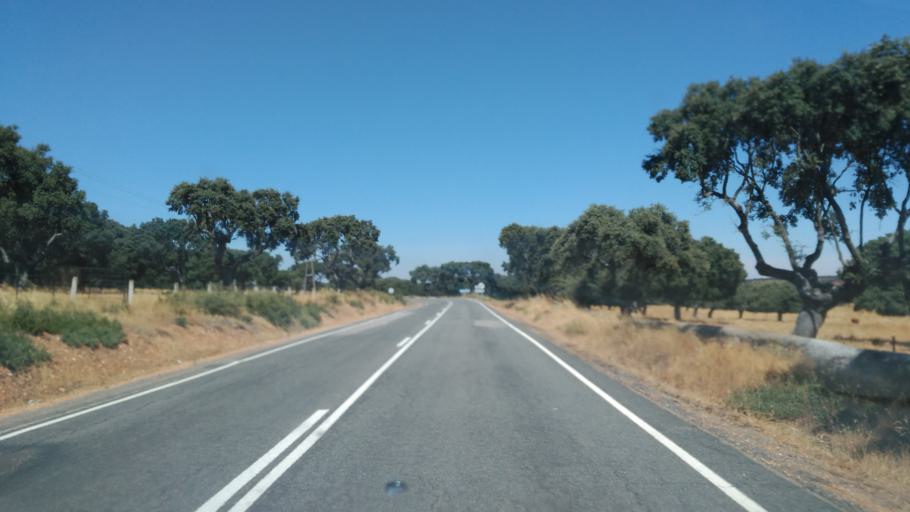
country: ES
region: Castille and Leon
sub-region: Provincia de Salamanca
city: Matilla de los Canos del Rio
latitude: 40.8036
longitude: -5.9238
